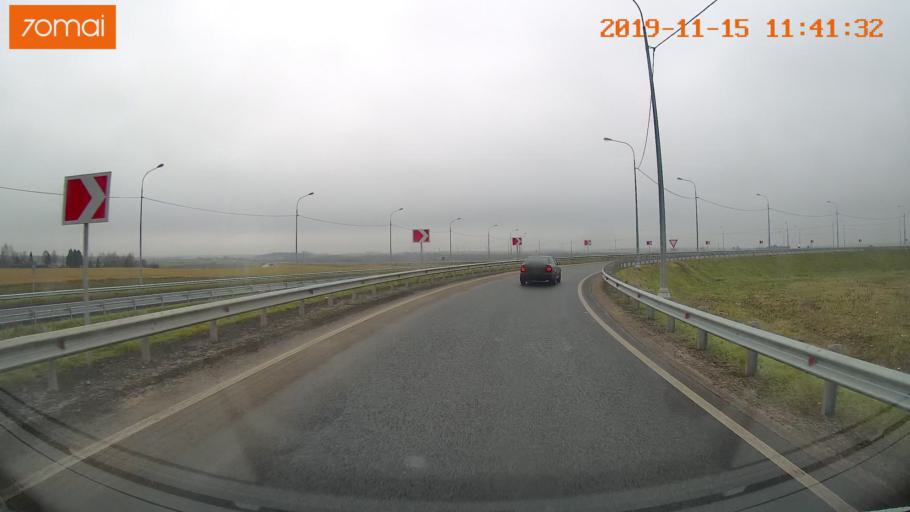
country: RU
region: Vologda
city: Vologda
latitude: 59.2122
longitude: 39.7706
